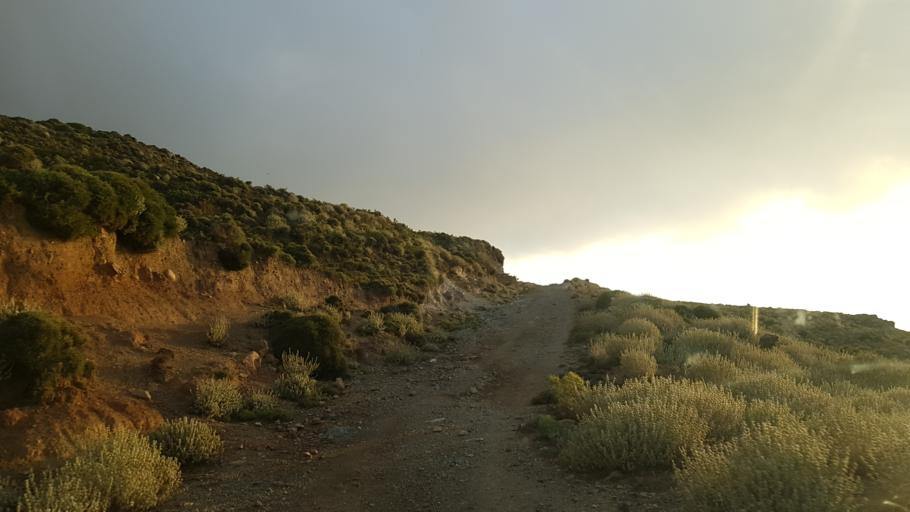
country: GR
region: Crete
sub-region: Nomos Chanias
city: Vryses
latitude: 35.4477
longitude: 23.5954
